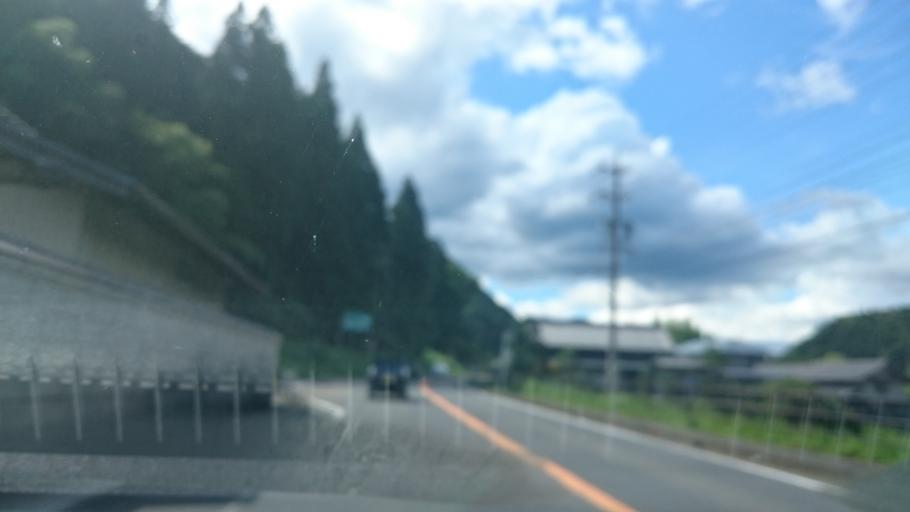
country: JP
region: Gifu
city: Nakatsugawa
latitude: 35.6310
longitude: 137.4523
